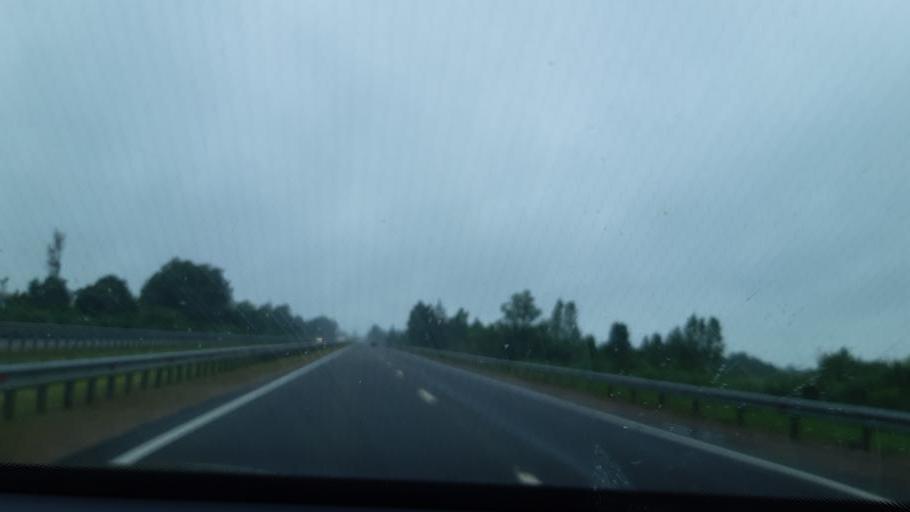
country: RU
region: Smolensk
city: Talashkino
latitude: 54.6648
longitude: 32.1550
